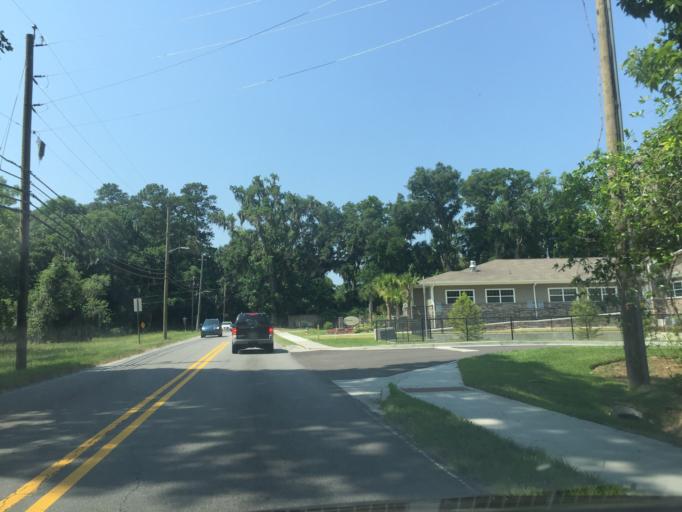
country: US
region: Georgia
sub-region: Chatham County
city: Montgomery
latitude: 31.9672
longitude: -81.1347
